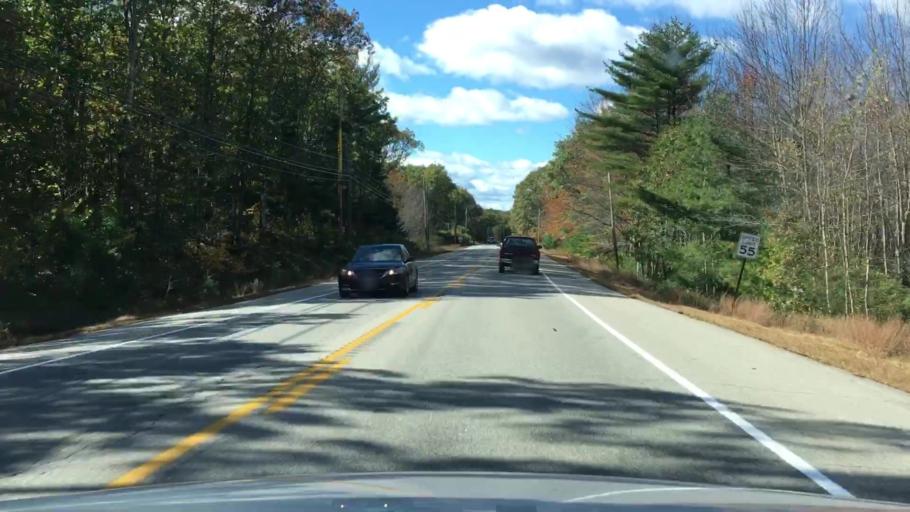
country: US
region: Maine
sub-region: York County
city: Alfred
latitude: 43.4763
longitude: -70.6630
